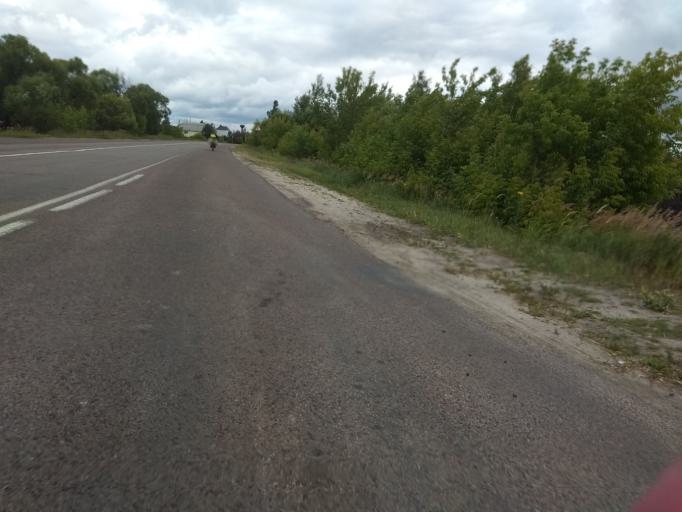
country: RU
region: Moskovskaya
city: Kerva
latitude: 55.5904
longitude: 39.7009
